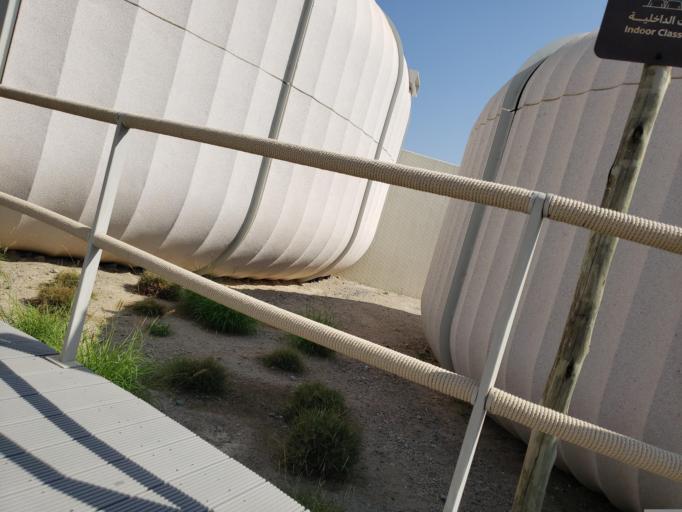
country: AE
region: Al Fujayrah
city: Al Fujayrah
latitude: 25.0130
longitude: 56.3616
